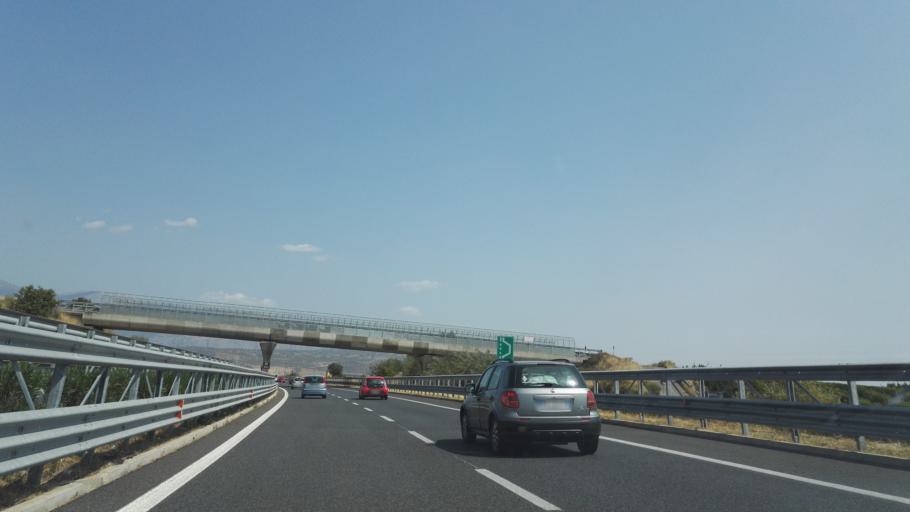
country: IT
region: Calabria
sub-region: Provincia di Cosenza
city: San Lorenzo del Vallo
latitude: 39.7064
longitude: 16.2435
